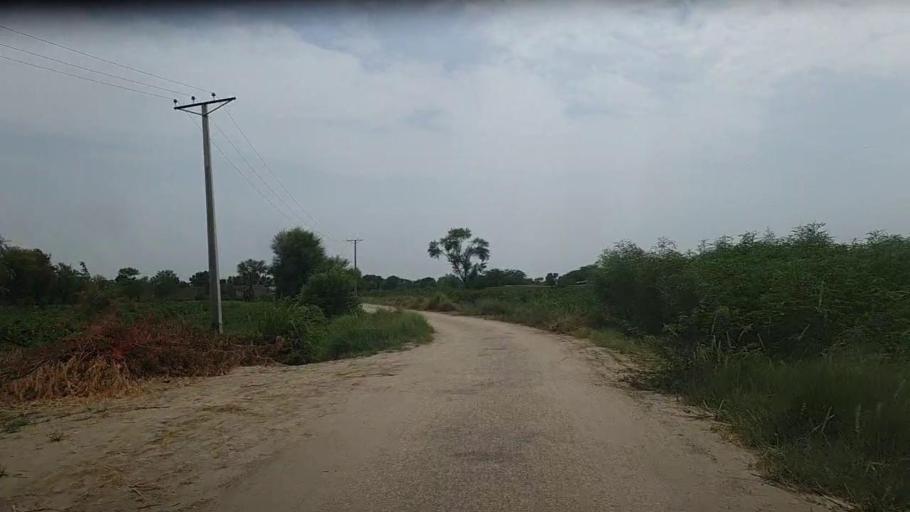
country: PK
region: Sindh
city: Bhiria
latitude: 26.8827
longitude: 68.2954
